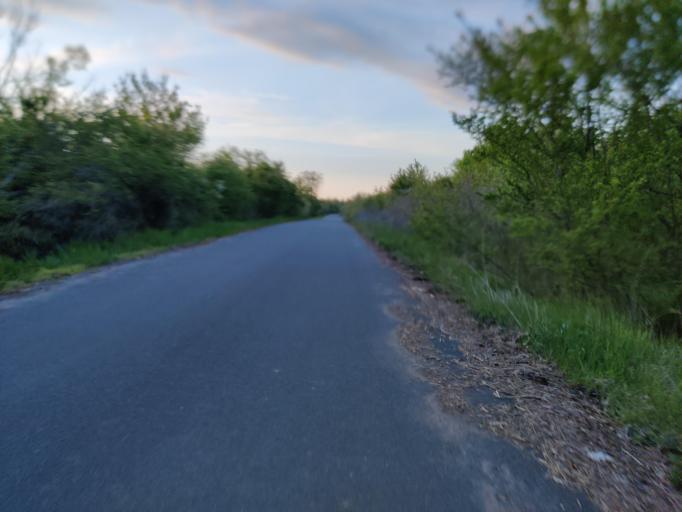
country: DE
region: Saxony
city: Markkleeberg
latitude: 51.2380
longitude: 12.3672
